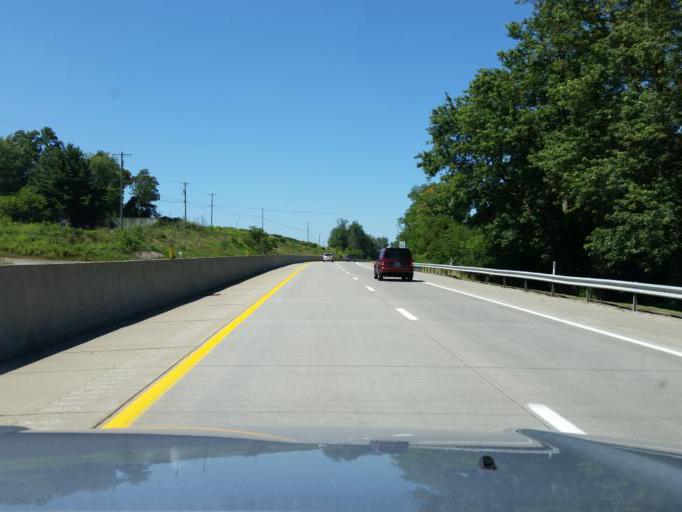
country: US
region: Pennsylvania
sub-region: Westmoreland County
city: Latrobe
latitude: 40.4133
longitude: -79.3802
